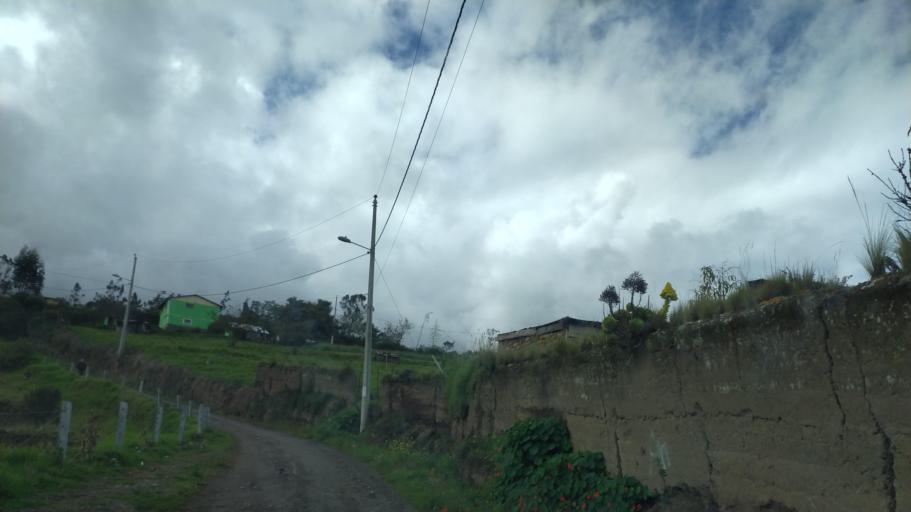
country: EC
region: Chimborazo
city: Riobamba
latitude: -1.6662
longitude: -78.5739
